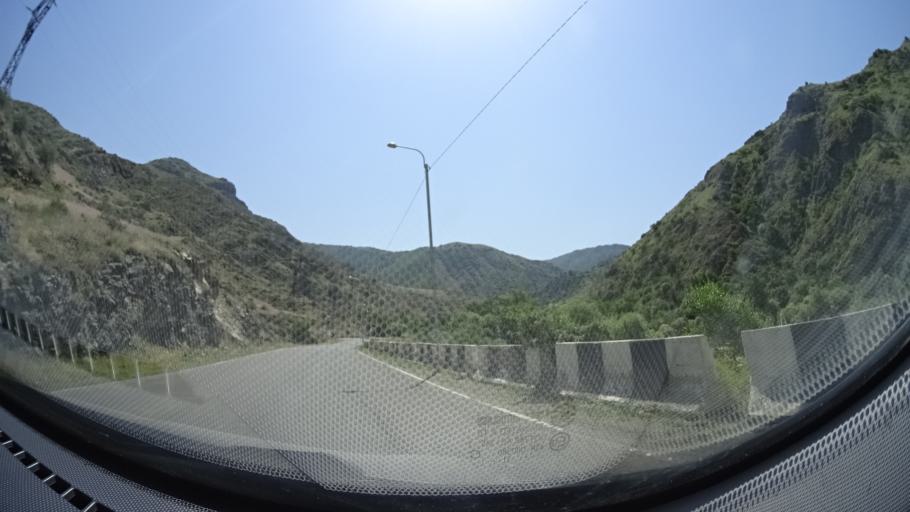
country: GE
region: Samtskhe-Javakheti
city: Aspindza
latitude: 41.5638
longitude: 43.2669
